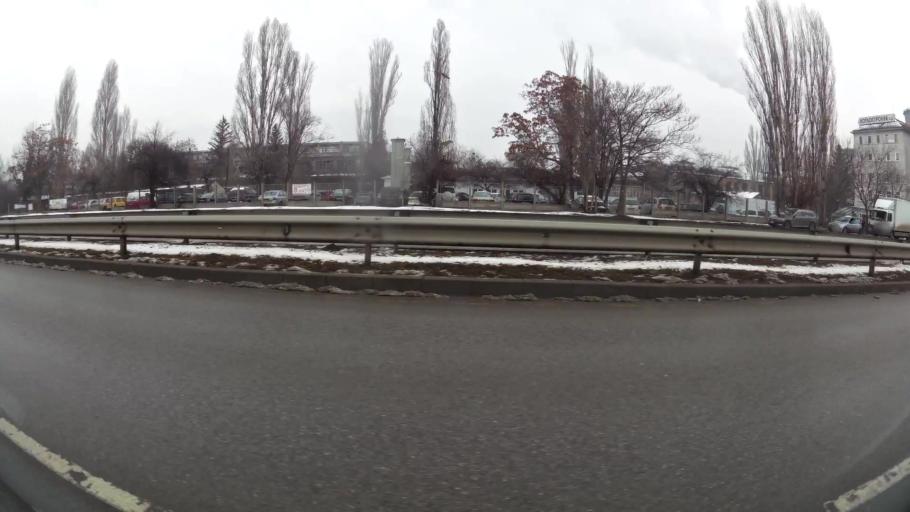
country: BG
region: Sofia-Capital
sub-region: Stolichna Obshtina
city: Sofia
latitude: 42.7183
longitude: 23.3170
